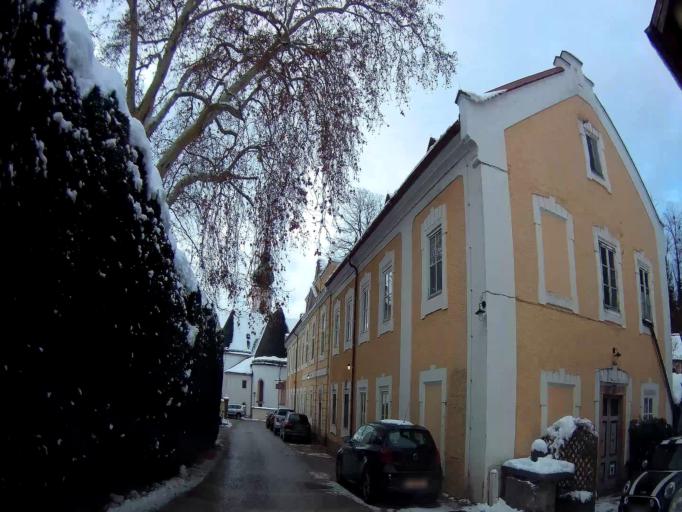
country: AT
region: Salzburg
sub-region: Politischer Bezirk Salzburg-Umgebung
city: Elsbethen
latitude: 47.7861
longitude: 13.0893
